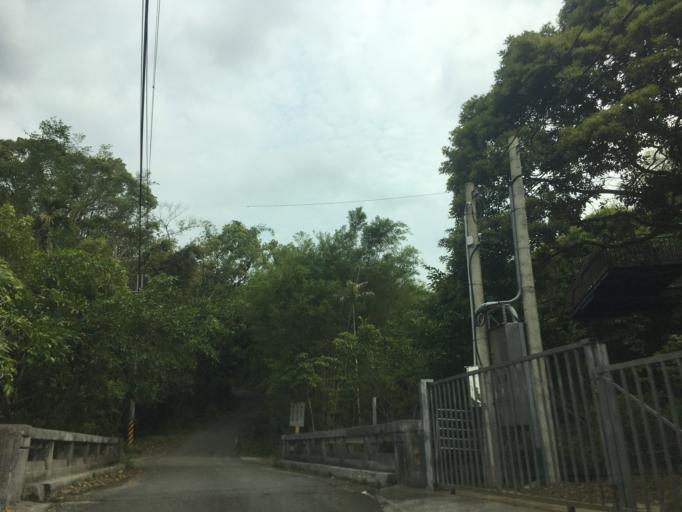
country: TW
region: Taiwan
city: Zhongxing New Village
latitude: 23.9844
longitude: 120.8143
